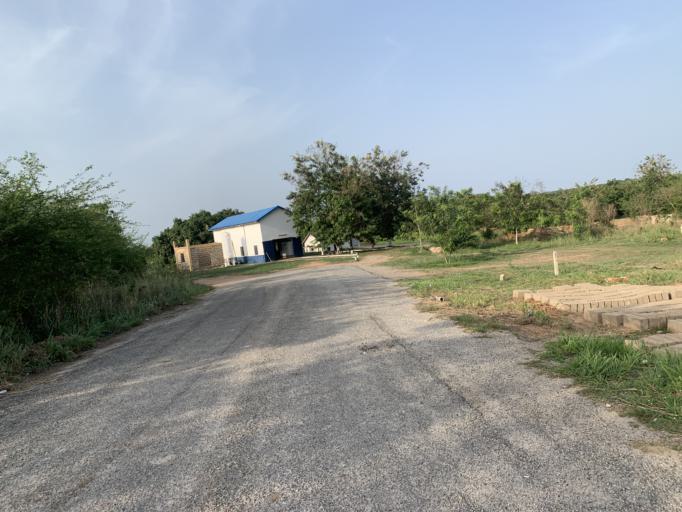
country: GH
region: Central
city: Winneba
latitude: 5.3916
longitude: -0.6013
